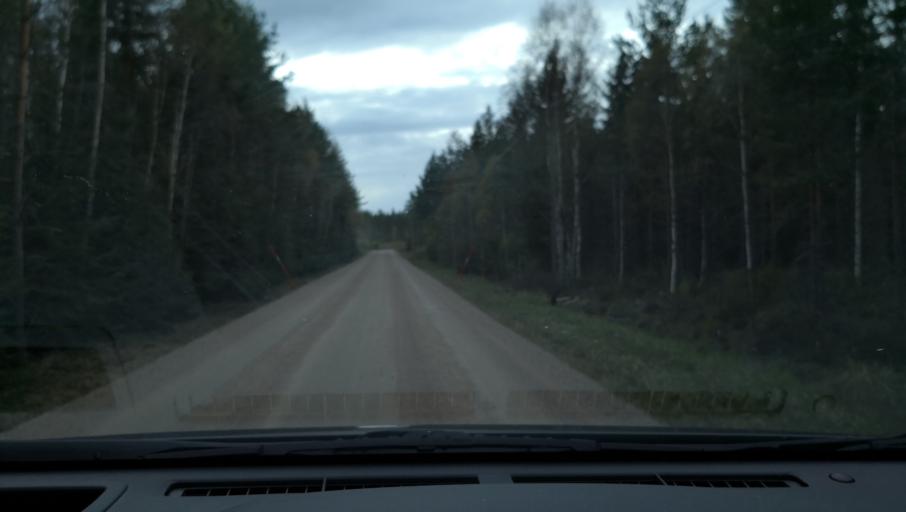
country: SE
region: Vaestmanland
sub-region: Fagersta Kommun
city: Fagersta
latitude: 60.1210
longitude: 15.7652
